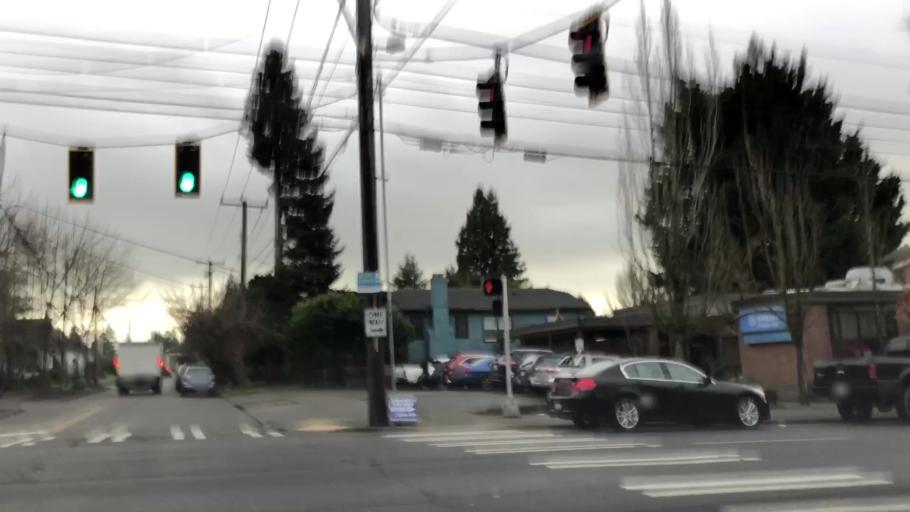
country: US
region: Washington
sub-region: King County
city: Seattle
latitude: 47.6816
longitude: -122.3176
